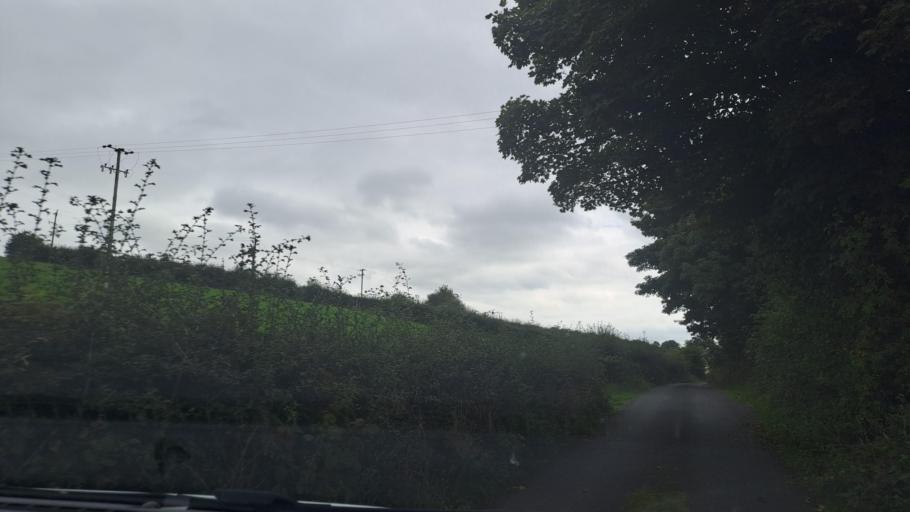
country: IE
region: Ulster
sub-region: An Cabhan
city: Kingscourt
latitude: 53.9725
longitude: -6.8478
